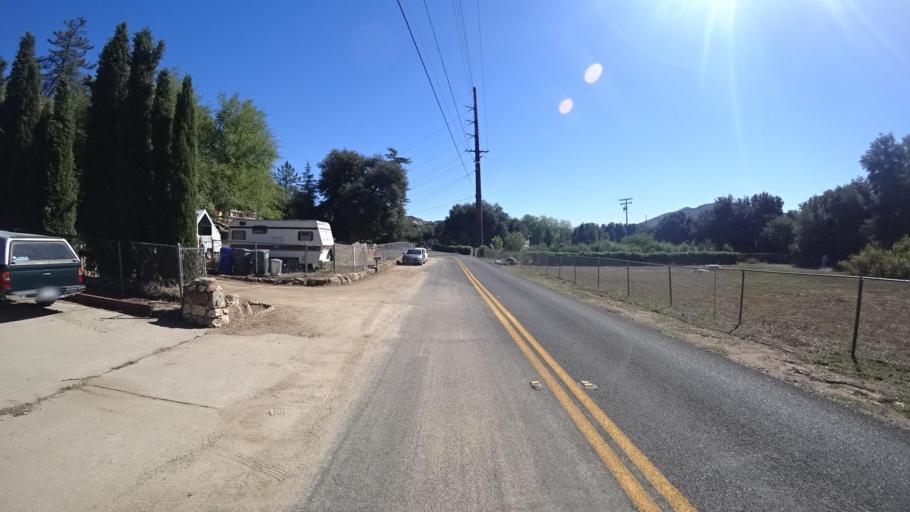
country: US
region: California
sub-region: San Diego County
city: Descanso
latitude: 32.8634
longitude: -116.6191
